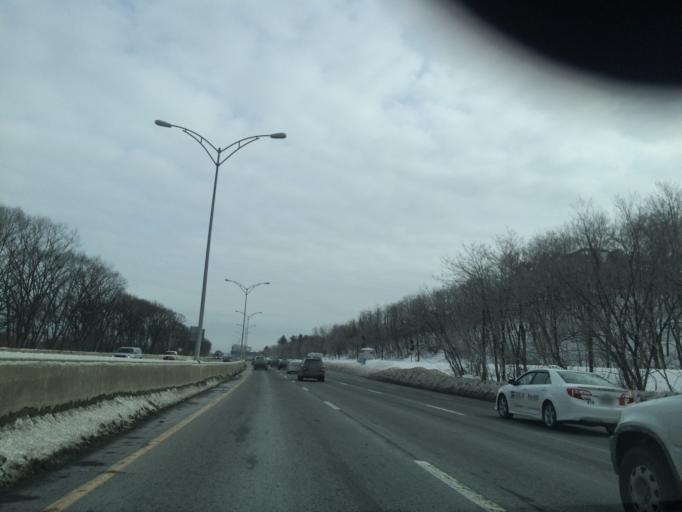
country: US
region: Massachusetts
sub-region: Middlesex County
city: Watertown
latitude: 42.3575
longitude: -71.1682
